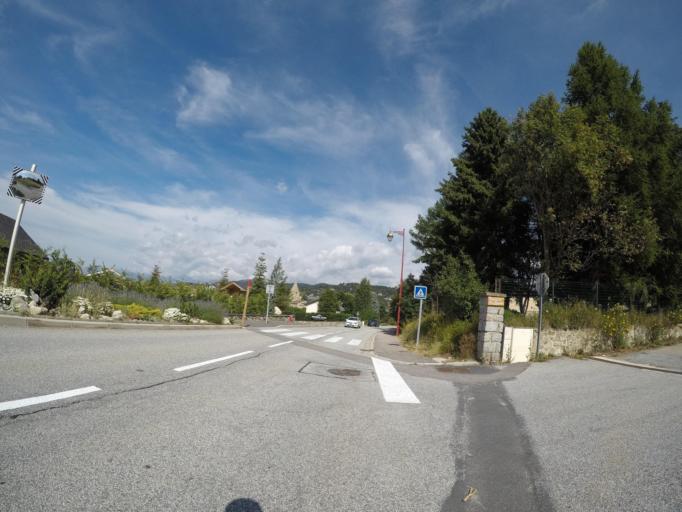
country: ES
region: Catalonia
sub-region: Provincia de Girona
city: Llivia
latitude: 42.5005
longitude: 2.0816
